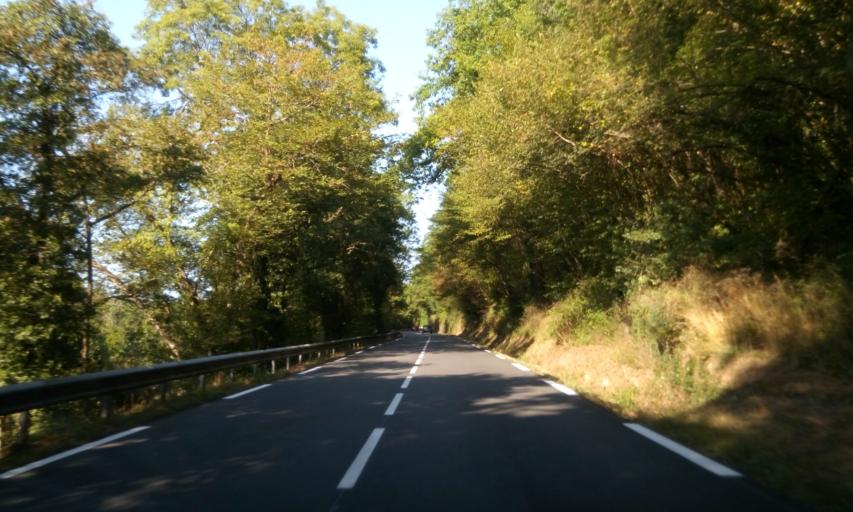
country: FR
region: Rhone-Alpes
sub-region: Departement du Rhone
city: Chatillon
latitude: 45.9068
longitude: 4.5890
